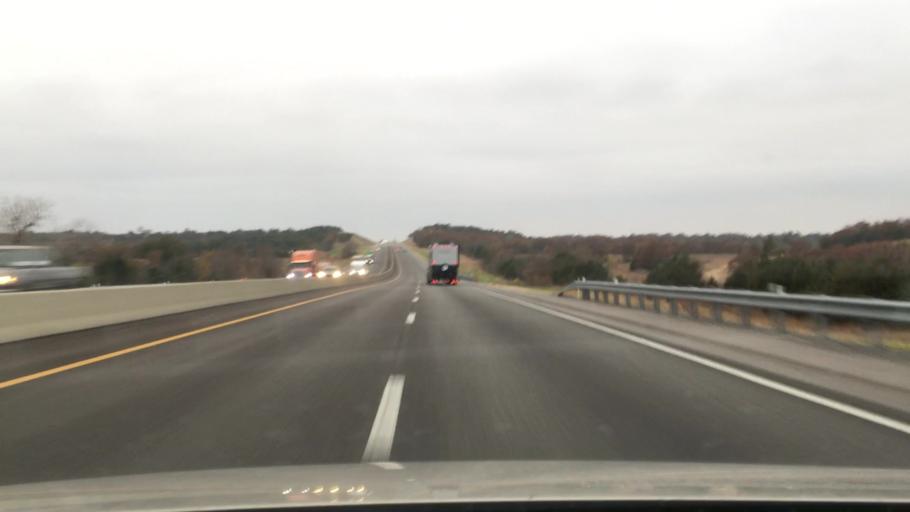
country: US
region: Oklahoma
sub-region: Lincoln County
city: Chandler
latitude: 35.7392
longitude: -96.7727
